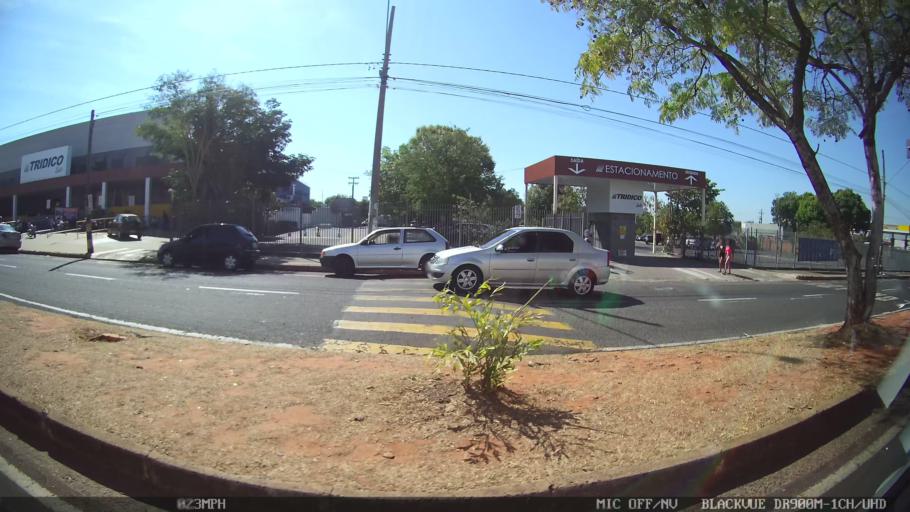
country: BR
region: Sao Paulo
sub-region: Sao Jose Do Rio Preto
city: Sao Jose do Rio Preto
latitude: -20.7744
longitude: -49.4139
